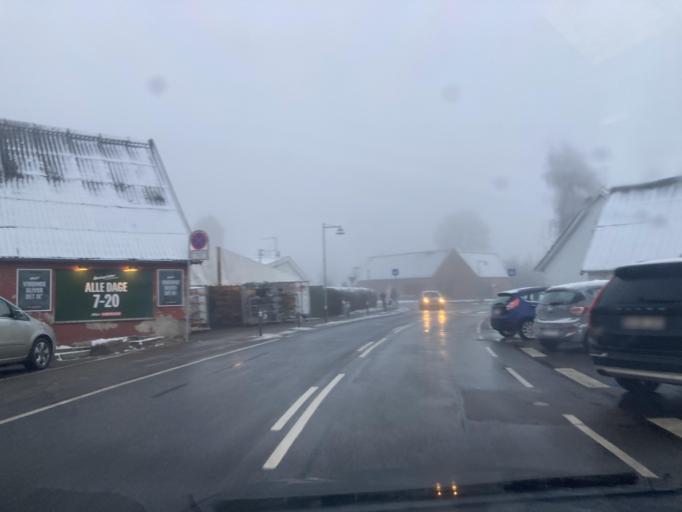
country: DK
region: Zealand
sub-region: Roskilde Kommune
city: Vindinge
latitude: 55.6258
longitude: 12.1354
